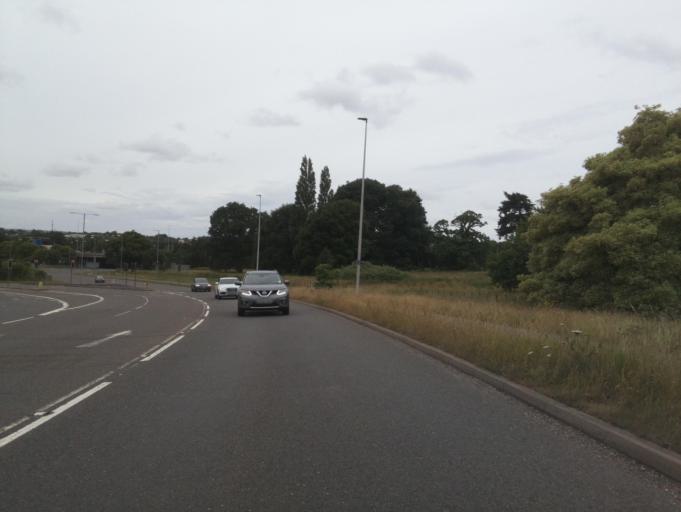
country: GB
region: England
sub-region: Devon
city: Heavitree
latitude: 50.7305
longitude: -3.4590
